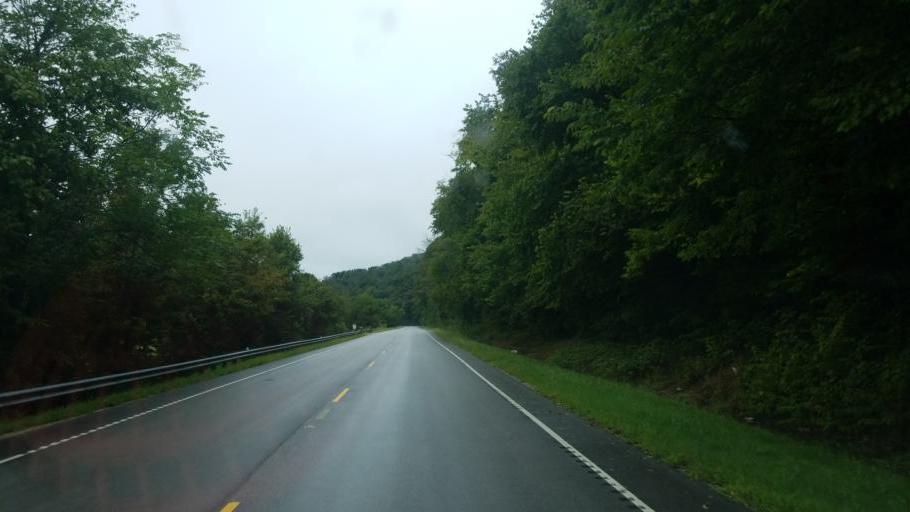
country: US
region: Ohio
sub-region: Adams County
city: Manchester
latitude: 38.6765
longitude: -83.6337
